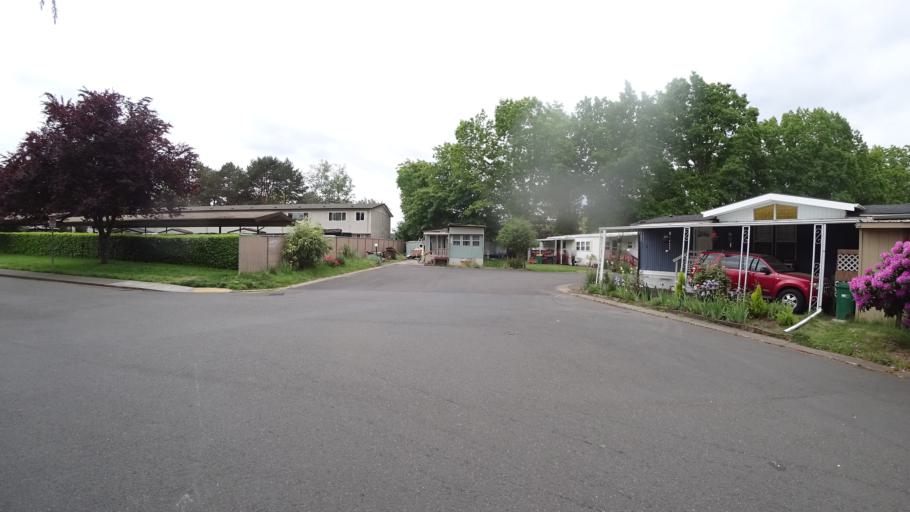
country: US
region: Oregon
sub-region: Washington County
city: Raleigh Hills
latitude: 45.4708
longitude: -122.7838
